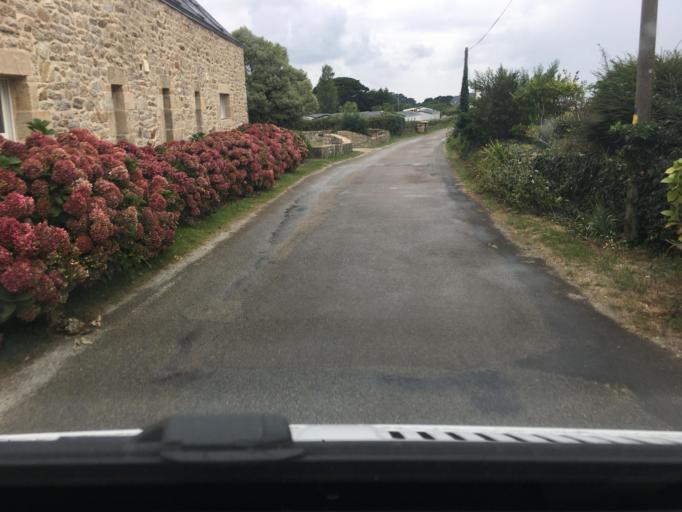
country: FR
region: Brittany
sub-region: Departement du Finistere
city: Beuzec-Cap-Sizun
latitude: 48.0838
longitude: -4.4792
